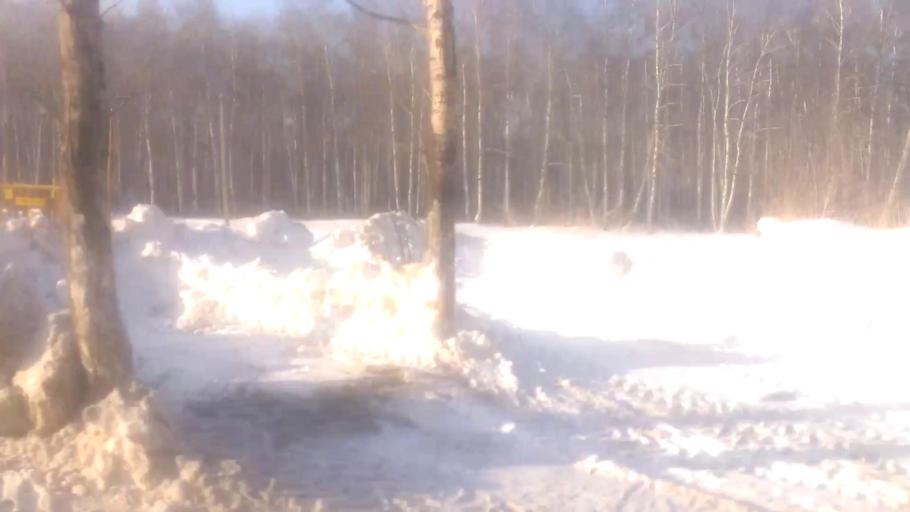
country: RU
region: Altai Krai
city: Novosilikatnyy
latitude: 53.3718
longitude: 83.6622
